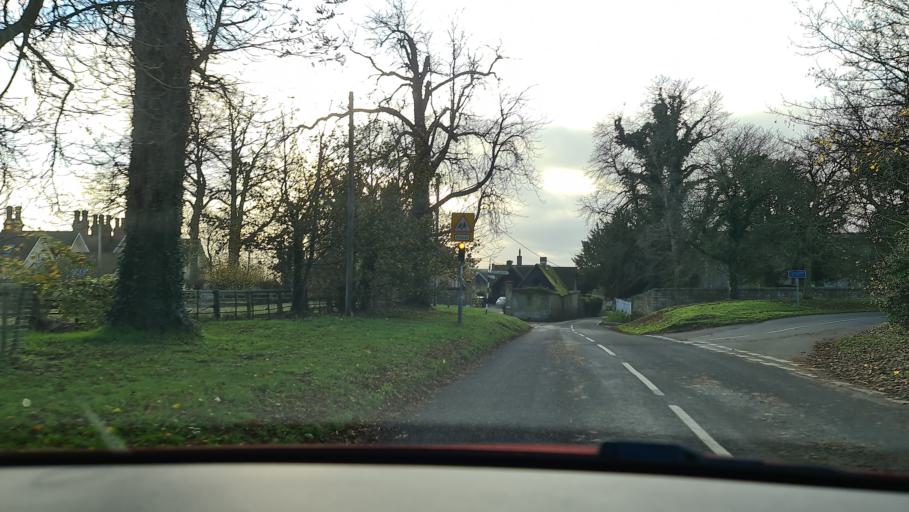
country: GB
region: England
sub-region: Buckinghamshire
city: Stone
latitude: 51.7941
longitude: -0.8896
